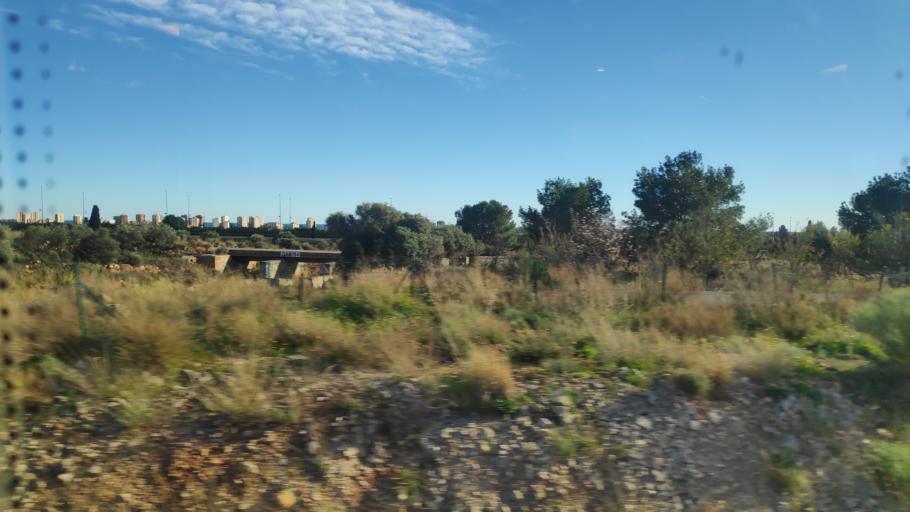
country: ES
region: Valencia
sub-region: Provincia de Castello
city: Benicassim
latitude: 40.0339
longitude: 0.0235
